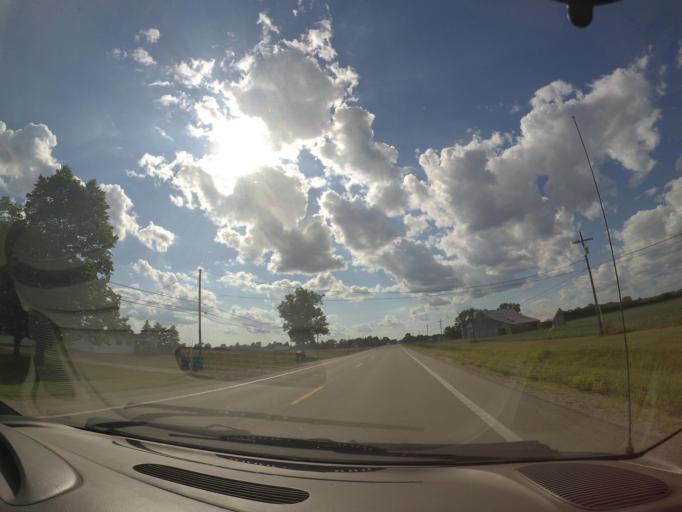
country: US
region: Ohio
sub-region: Wood County
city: Luckey
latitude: 41.5003
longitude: -83.4846
